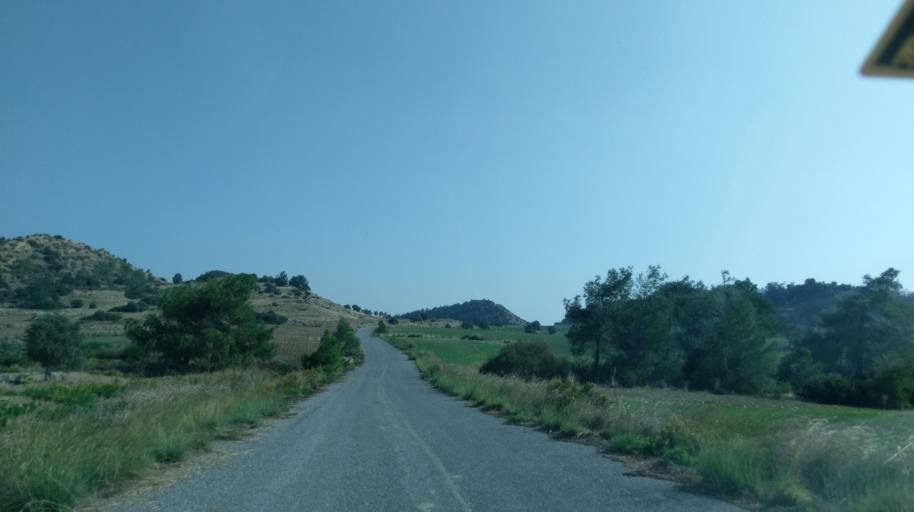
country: CY
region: Ammochostos
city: Lefkonoiko
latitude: 35.3216
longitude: 33.6691
